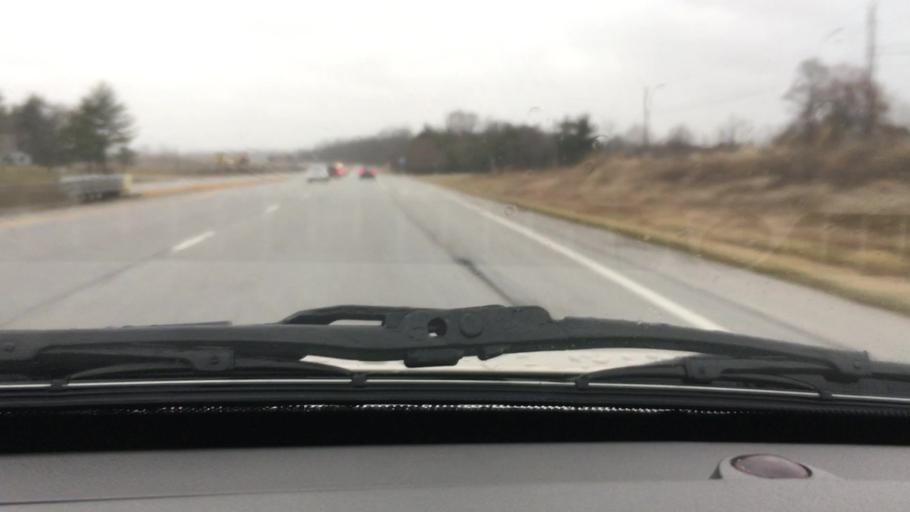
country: US
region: Indiana
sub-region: Delaware County
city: Yorktown
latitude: 40.2198
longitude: -85.5175
